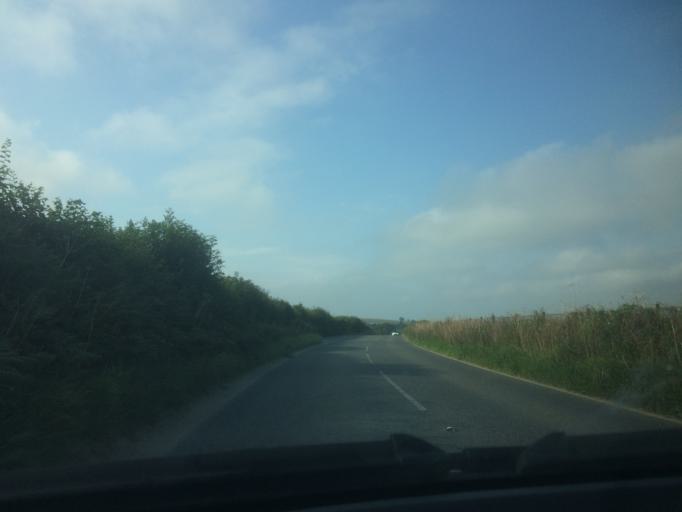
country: GB
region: England
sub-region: Cornwall
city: Saltash
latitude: 50.4258
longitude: -4.2589
